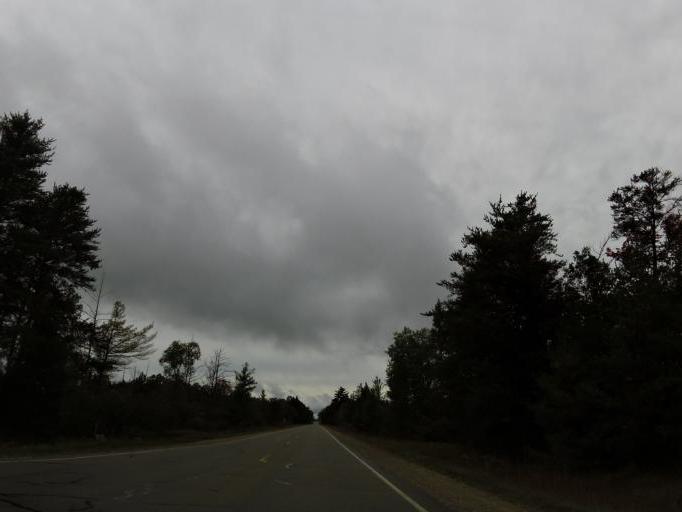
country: US
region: Michigan
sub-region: Roscommon County
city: Roscommon
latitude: 44.4867
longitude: -84.5723
